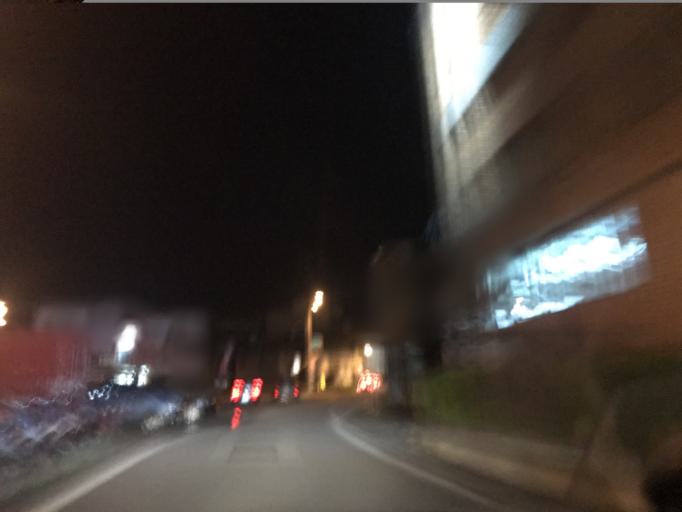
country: TW
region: Taiwan
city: Daxi
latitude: 24.8624
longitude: 121.2122
